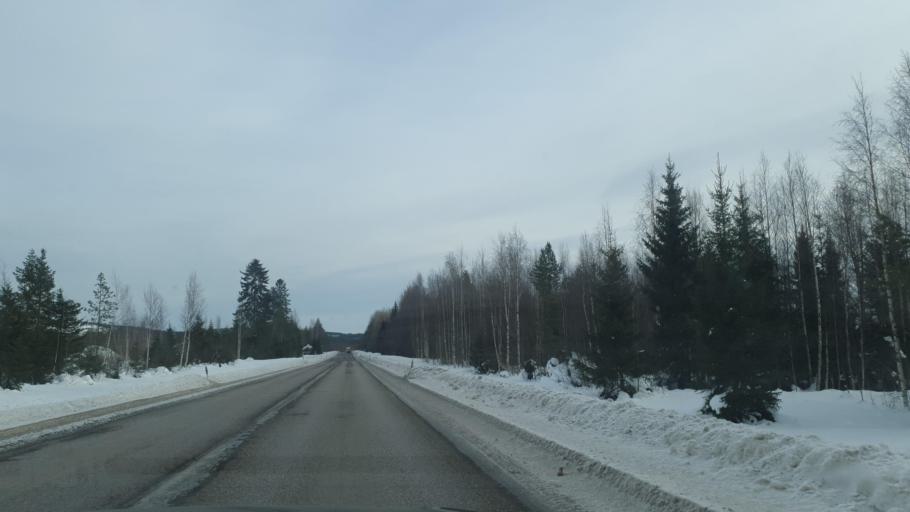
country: FI
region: Kainuu
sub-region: Kajaani
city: Kajaani
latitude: 64.4700
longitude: 27.4658
